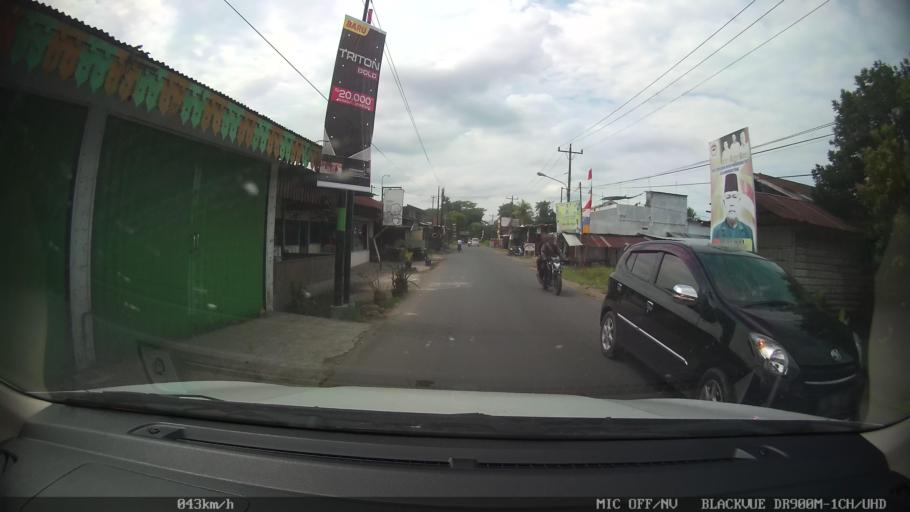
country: ID
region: North Sumatra
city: Sunggal
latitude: 3.6335
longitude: 98.5937
